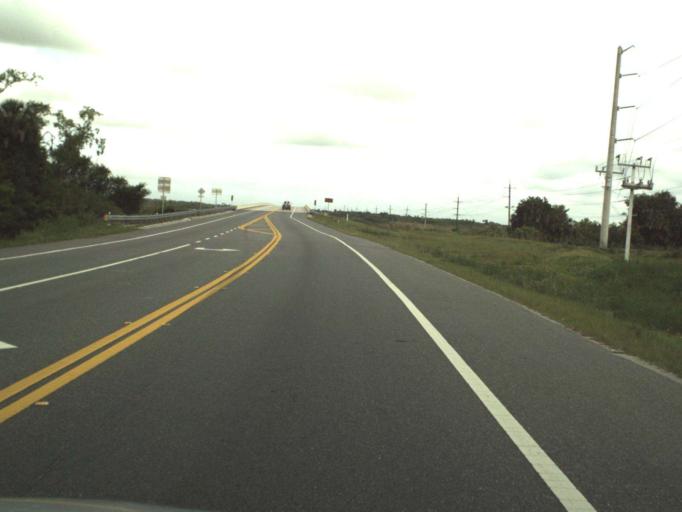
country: US
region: Florida
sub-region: Seminole County
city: Midway
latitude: 28.7810
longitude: -81.1687
